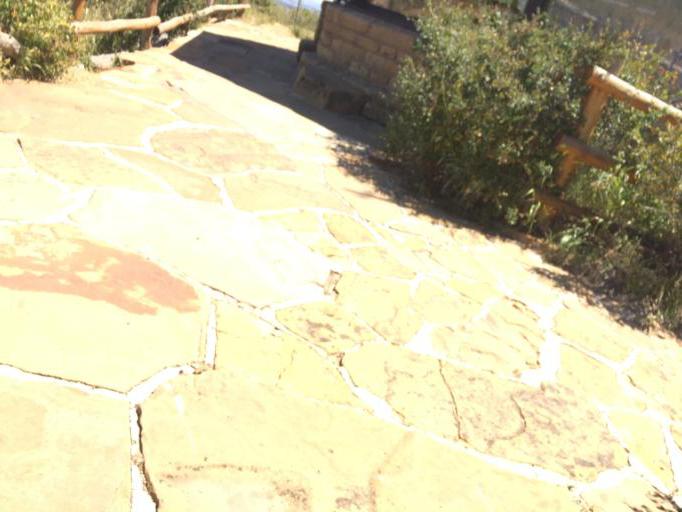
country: US
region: Colorado
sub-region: Montezuma County
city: Cortez
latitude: 37.2807
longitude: -108.4615
